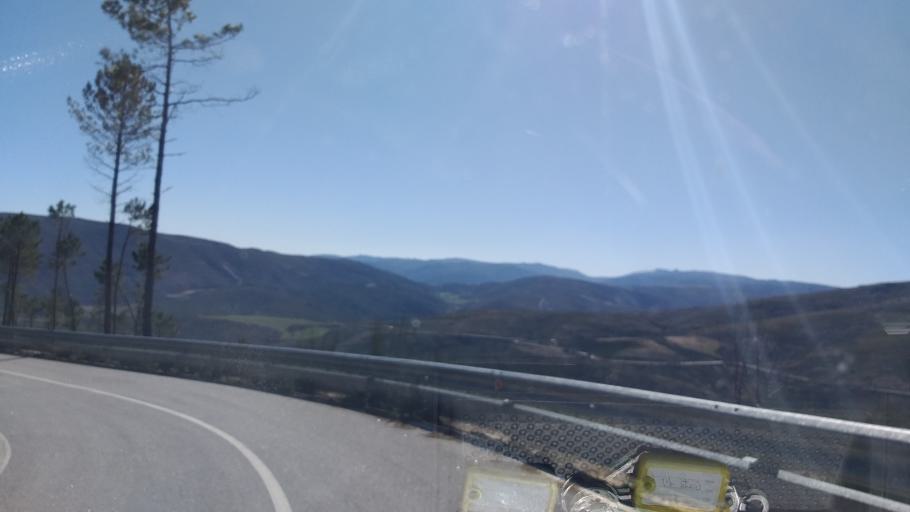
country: PT
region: Guarda
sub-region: Manteigas
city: Manteigas
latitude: 40.4755
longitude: -7.5090
